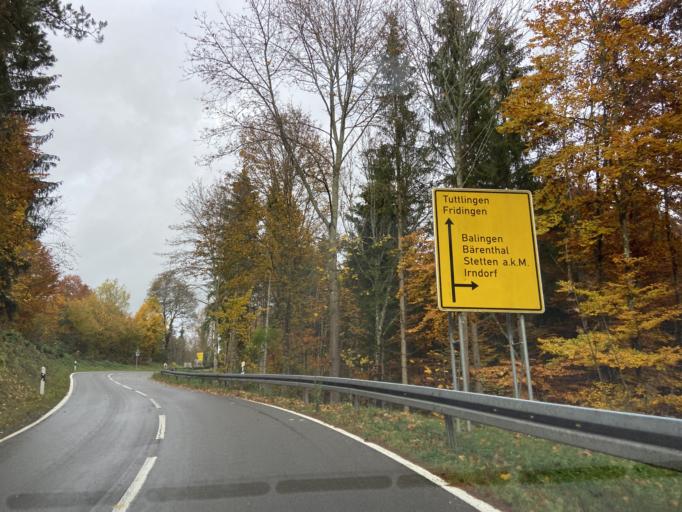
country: DE
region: Baden-Wuerttemberg
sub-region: Tuebingen Region
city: Beuron
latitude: 48.0462
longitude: 8.9519
